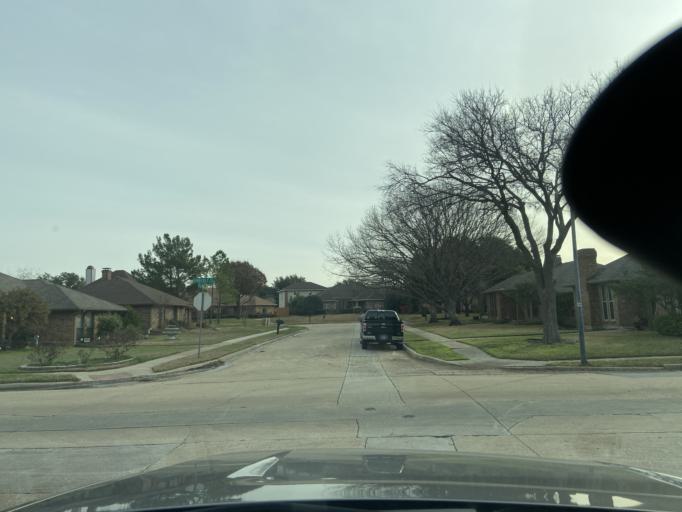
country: US
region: Texas
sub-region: Dallas County
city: Carrollton
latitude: 33.0037
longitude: -96.9051
